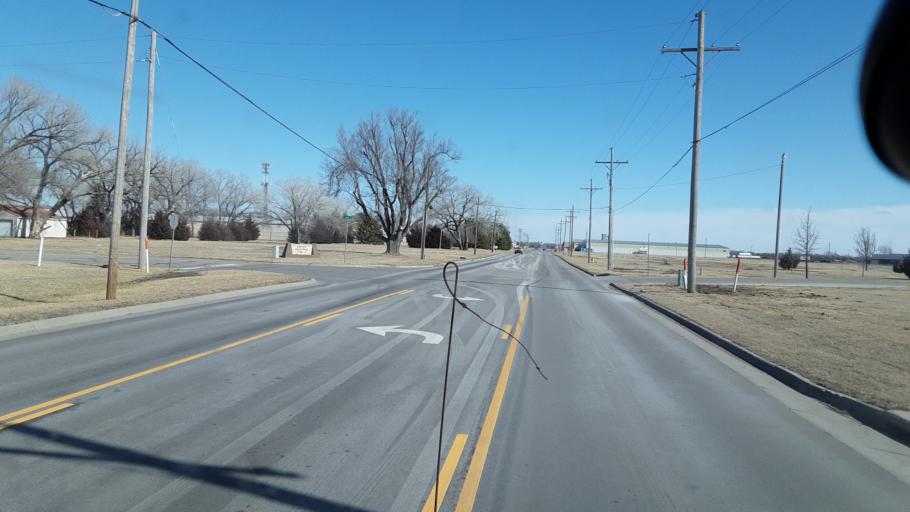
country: US
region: Kansas
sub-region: Reno County
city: Hutchinson
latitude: 38.0576
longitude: -97.8746
